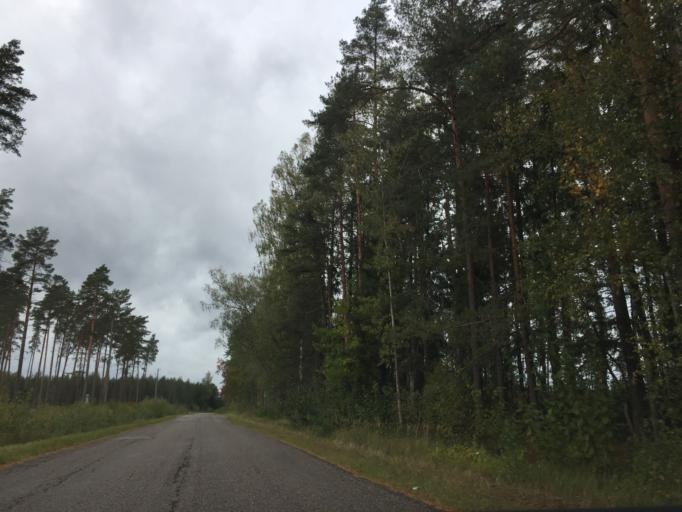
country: LV
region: Olaine
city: Olaine
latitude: 56.7647
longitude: 23.8890
